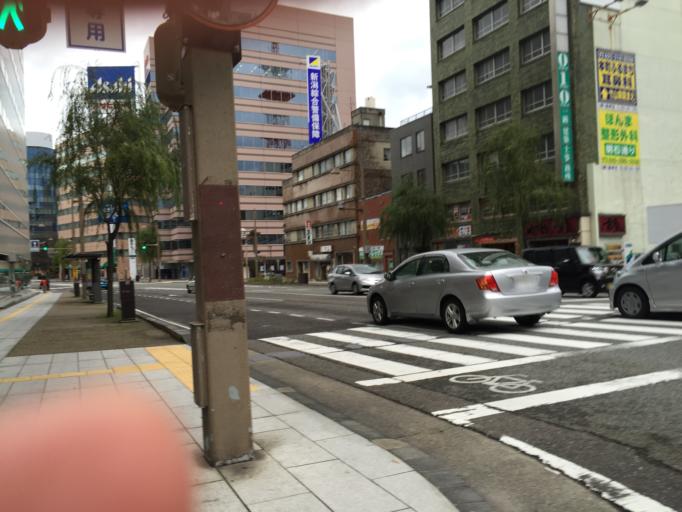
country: JP
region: Niigata
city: Niigata-shi
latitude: 37.9206
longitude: 139.0509
